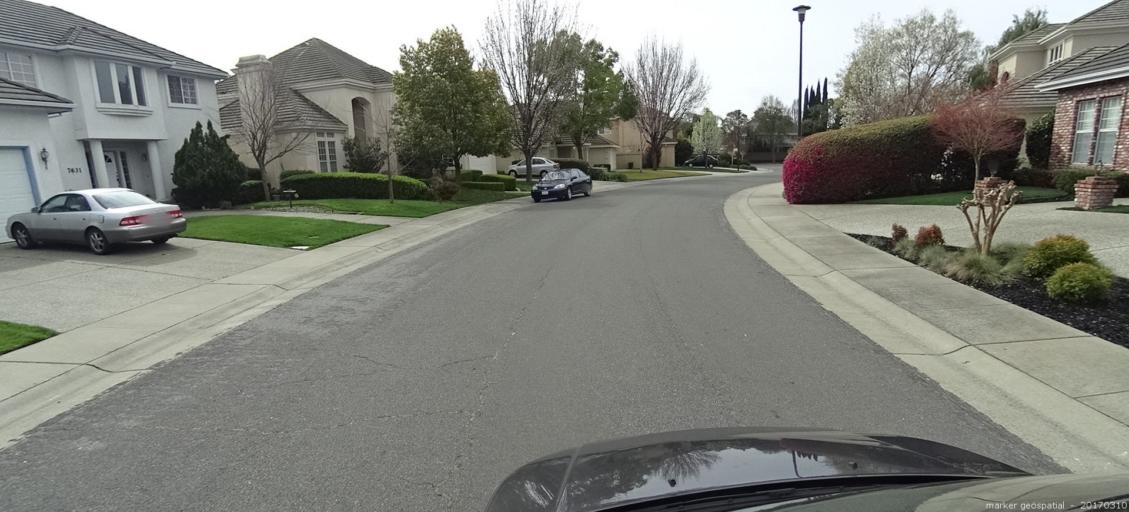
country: US
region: California
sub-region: Sacramento County
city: Parkway
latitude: 38.4845
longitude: -121.5283
